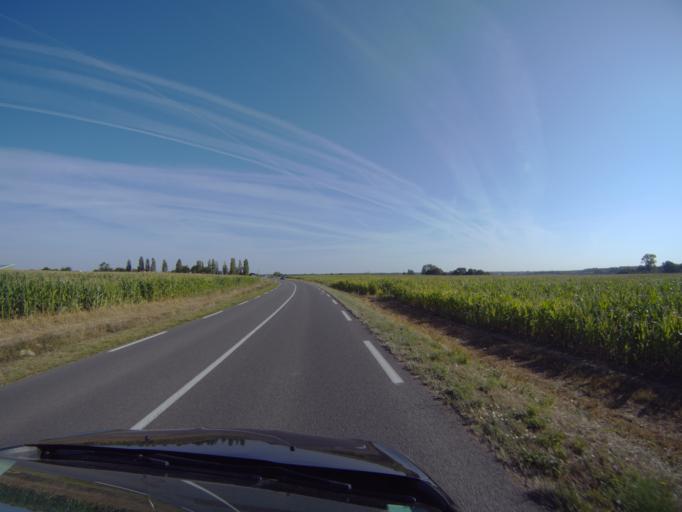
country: FR
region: Pays de la Loire
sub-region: Departement de la Vendee
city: Jard-sur-Mer
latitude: 46.4390
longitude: -1.5785
